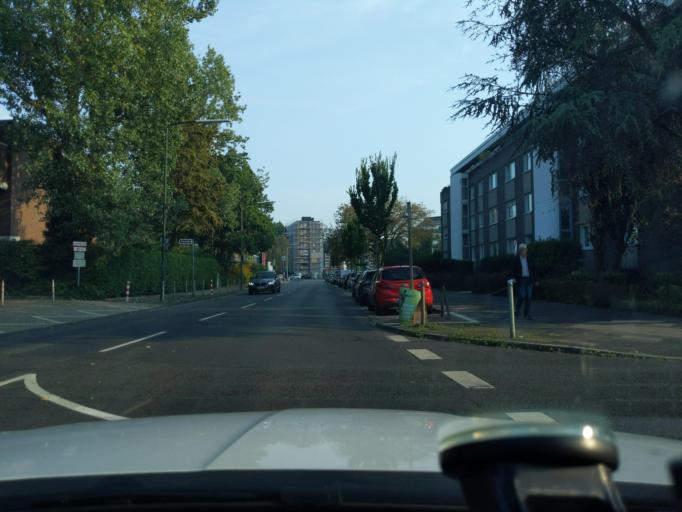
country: DE
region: North Rhine-Westphalia
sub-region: Regierungsbezirk Dusseldorf
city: Dusseldorf
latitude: 51.2353
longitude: 6.8156
